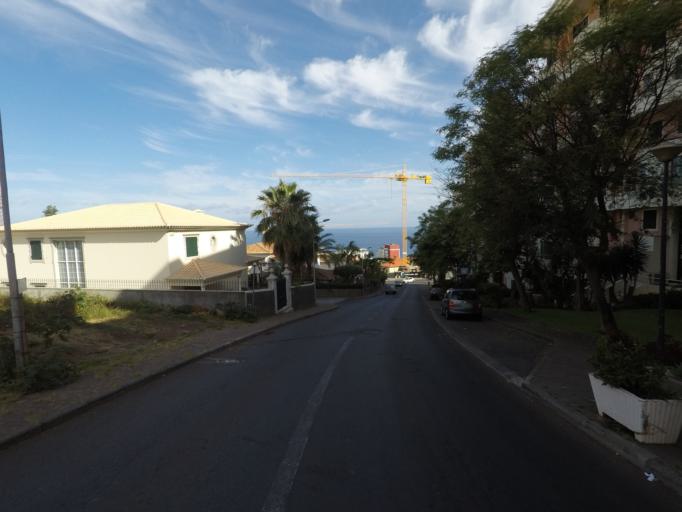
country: PT
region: Madeira
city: Camara de Lobos
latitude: 32.6382
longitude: -16.9409
